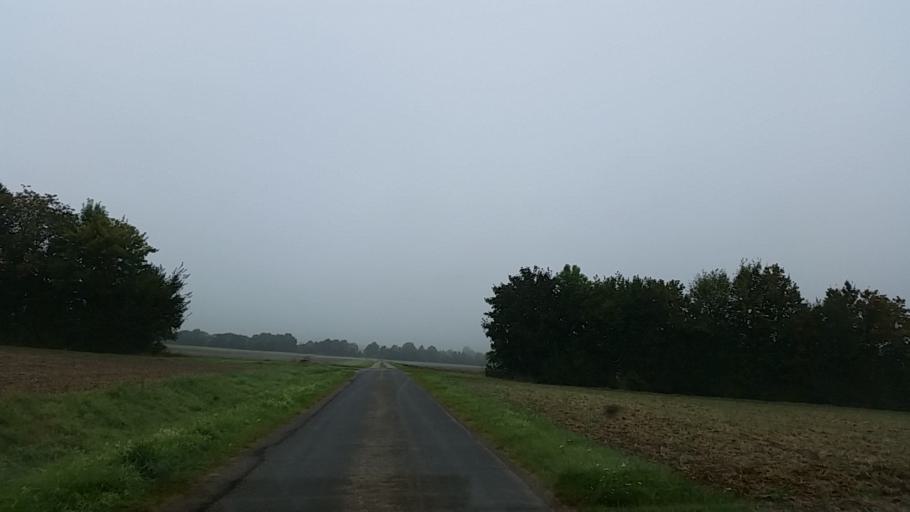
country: DE
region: Bavaria
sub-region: Regierungsbezirk Unterfranken
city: Himmelstadt
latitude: 49.9374
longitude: 9.7977
